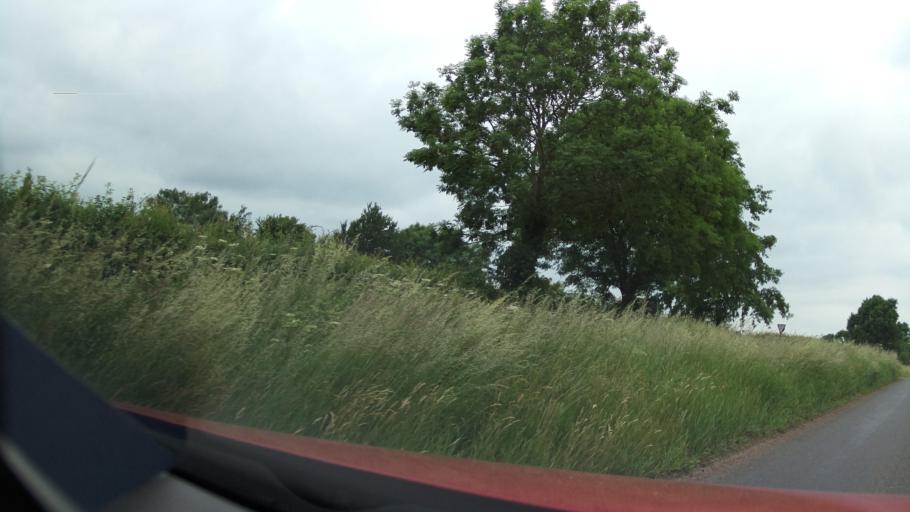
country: GB
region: England
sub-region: District of Rutland
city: Uppingham
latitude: 52.5991
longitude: -0.7230
